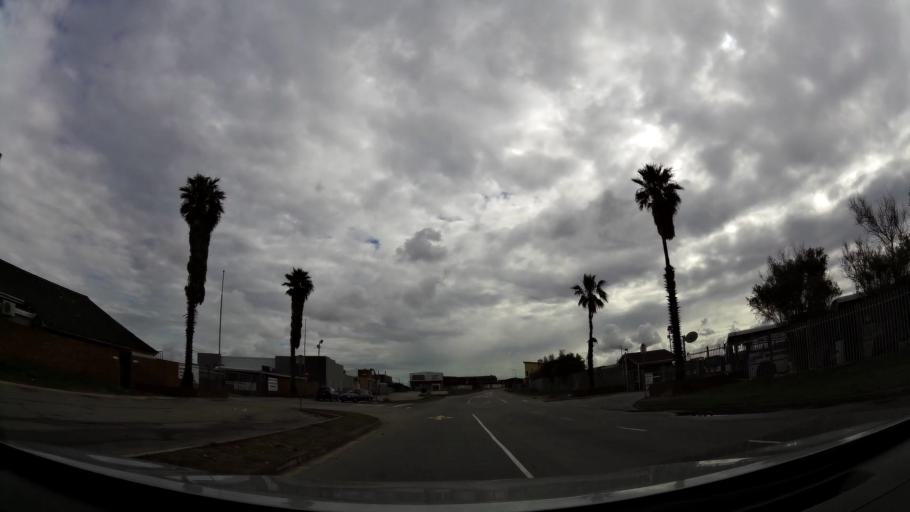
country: ZA
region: Eastern Cape
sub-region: Nelson Mandela Bay Metropolitan Municipality
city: Port Elizabeth
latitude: -33.9304
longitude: 25.5847
